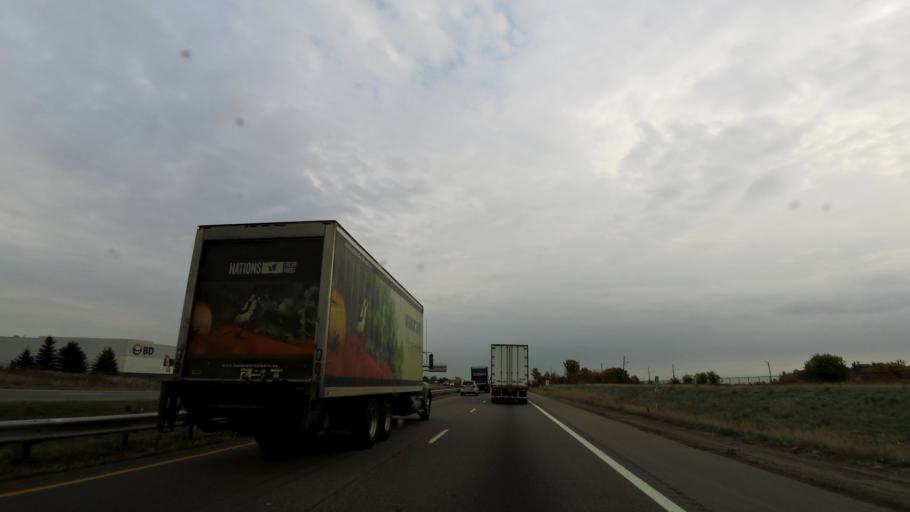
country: CA
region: Ontario
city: Oakville
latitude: 43.5077
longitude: -79.6863
